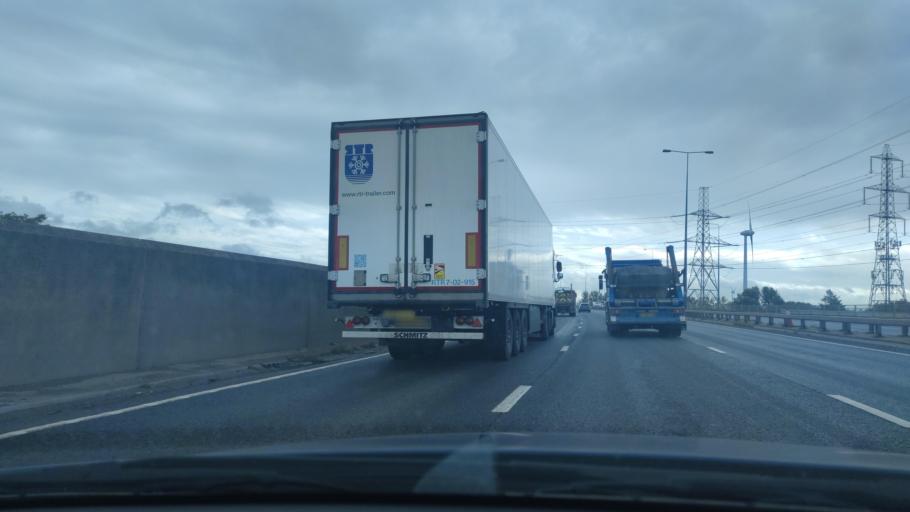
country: GB
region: England
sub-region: Greater London
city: Becontree
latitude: 51.5263
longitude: 0.1453
